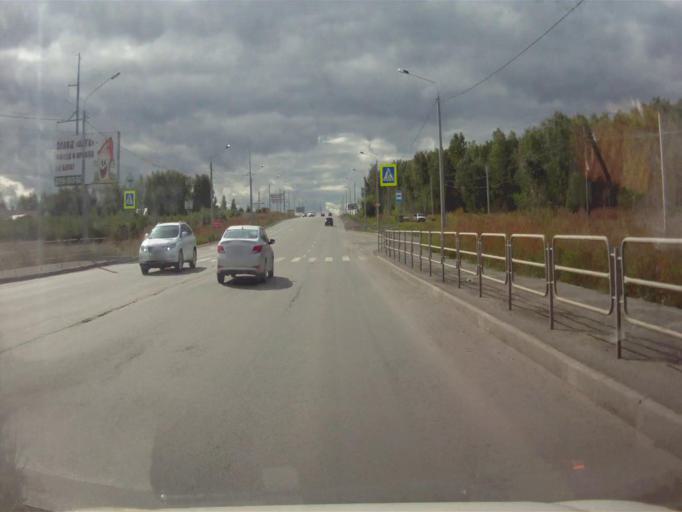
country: RU
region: Chelyabinsk
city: Sargazy
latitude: 55.1436
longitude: 61.2762
